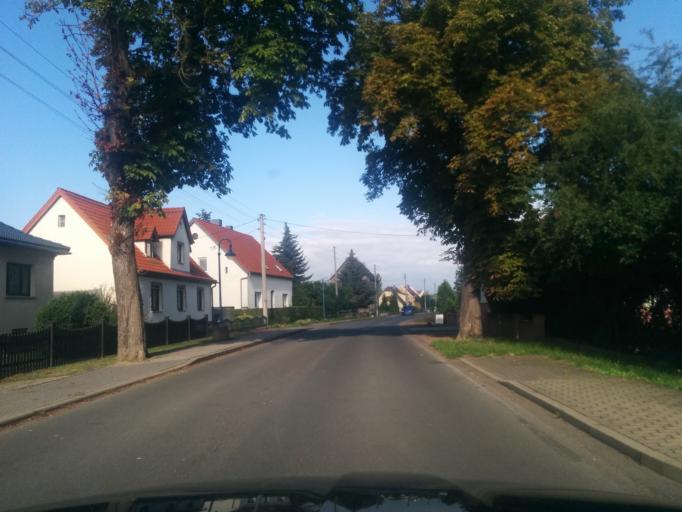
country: DE
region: Saxony-Anhalt
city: Bennstedt
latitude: 51.4803
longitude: 11.8288
